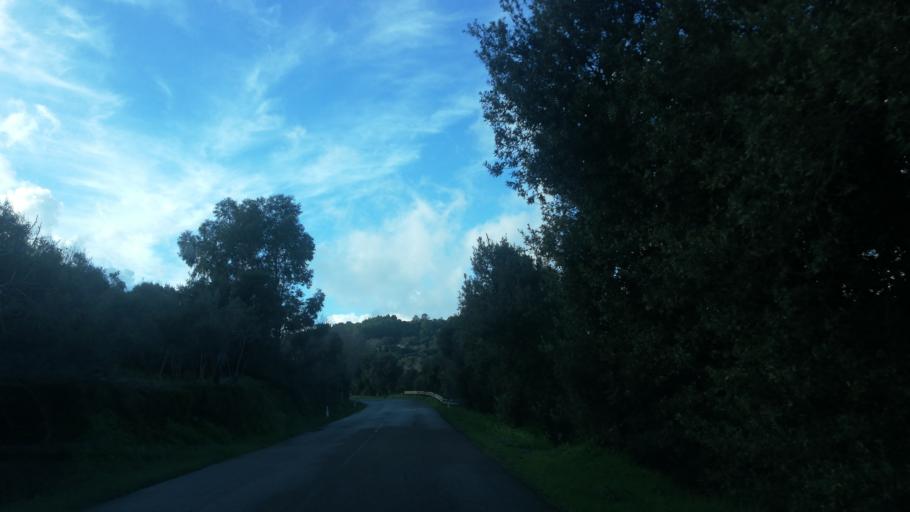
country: IT
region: Sardinia
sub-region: Provincia di Medio Campidano
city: Villanovaforru
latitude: 39.6334
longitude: 8.8622
